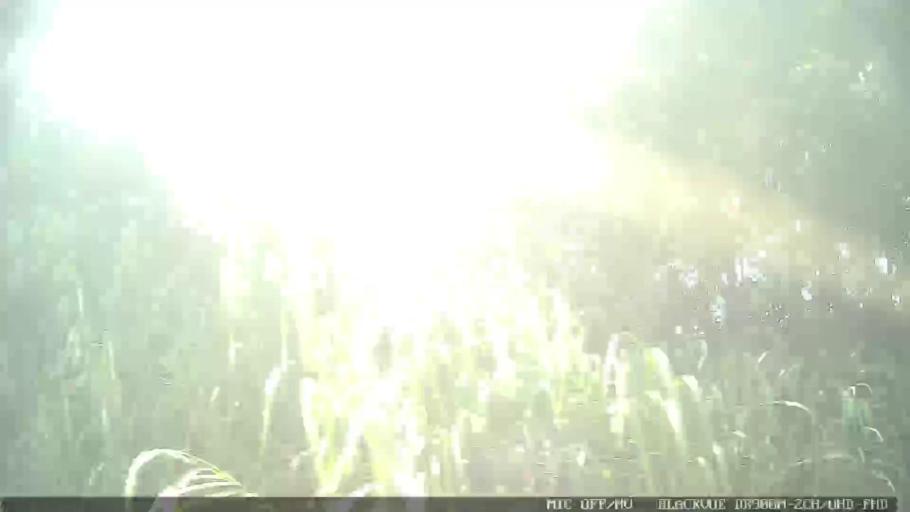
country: BR
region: Sao Paulo
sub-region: Jarinu
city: Jarinu
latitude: -23.1068
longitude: -46.6509
